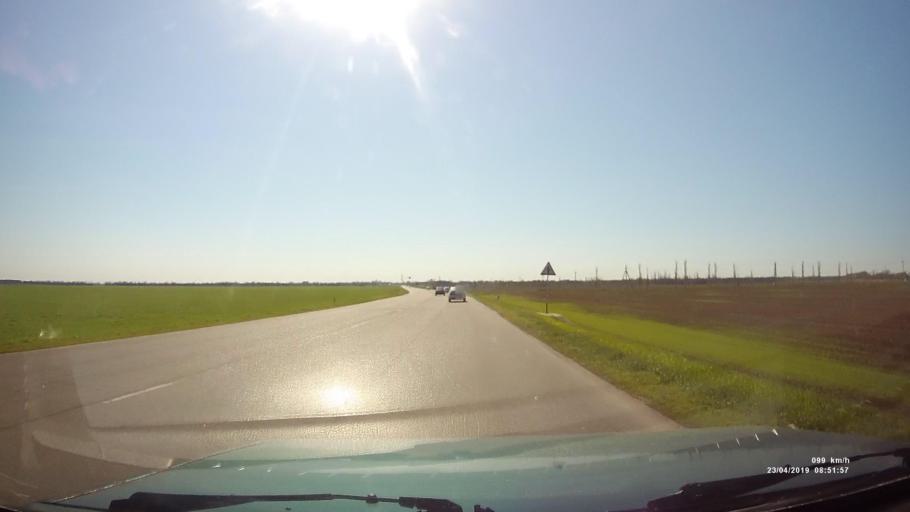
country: RU
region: Rostov
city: Sal'sk
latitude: 46.4845
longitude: 41.4511
